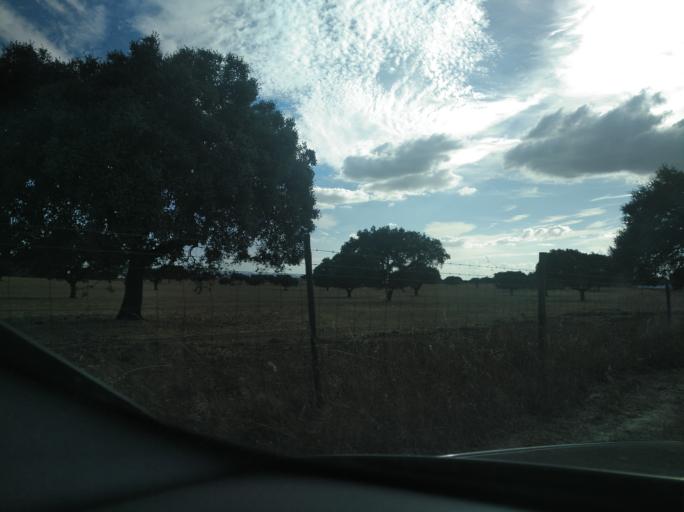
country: PT
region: Portalegre
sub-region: Campo Maior
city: Campo Maior
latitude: 39.0699
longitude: -7.1120
